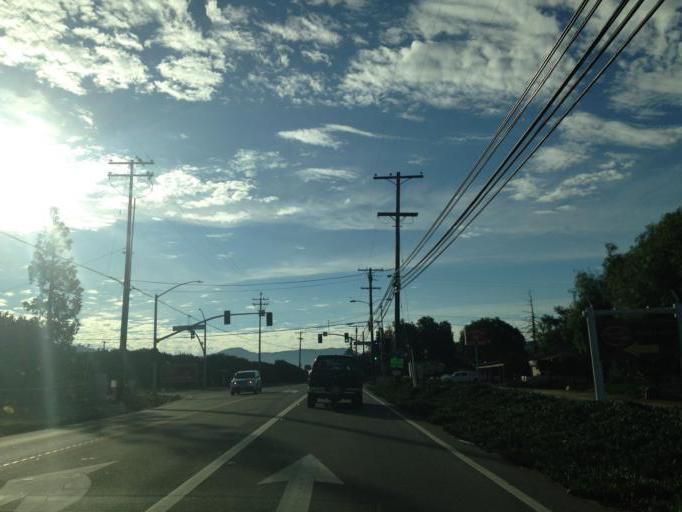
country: US
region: California
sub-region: San Diego County
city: Valley Center
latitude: 33.3303
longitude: -117.0013
